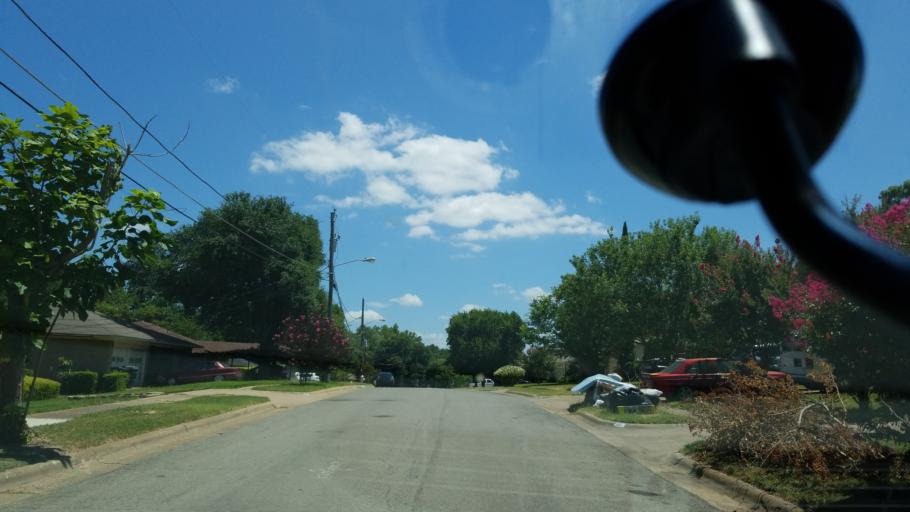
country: US
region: Texas
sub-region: Dallas County
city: Cockrell Hill
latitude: 32.6928
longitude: -96.8192
